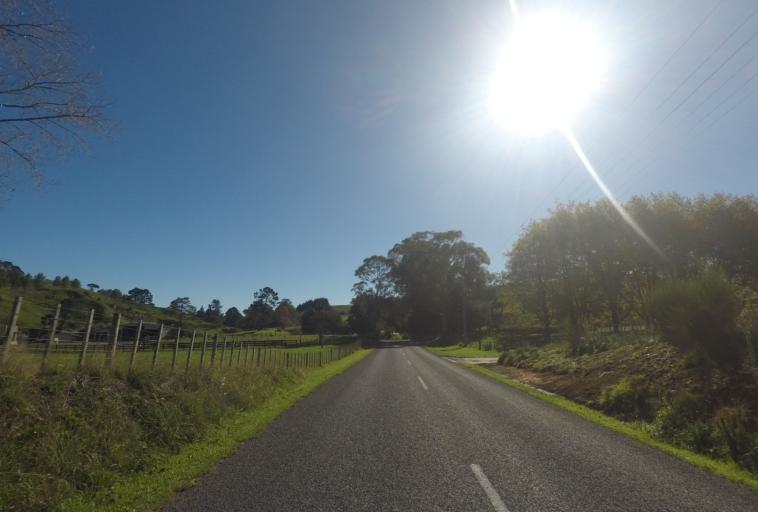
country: NZ
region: Bay of Plenty
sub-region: Western Bay of Plenty District
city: Waihi Beach
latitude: -37.3985
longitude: 175.9065
